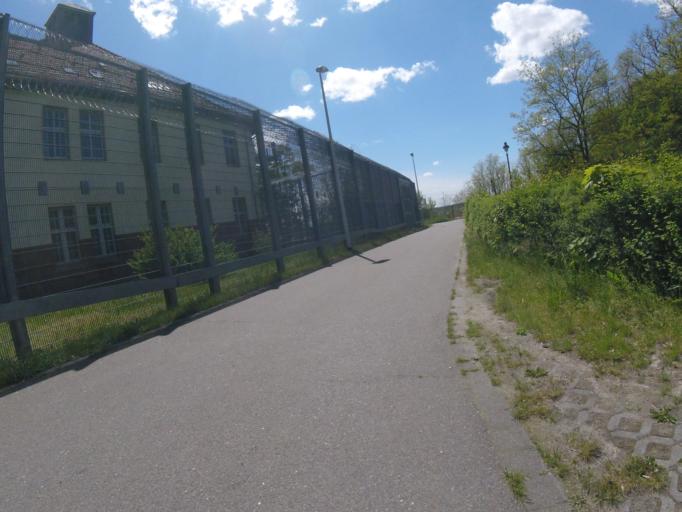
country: DE
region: Brandenburg
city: Teupitz
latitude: 52.1295
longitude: 13.6173
